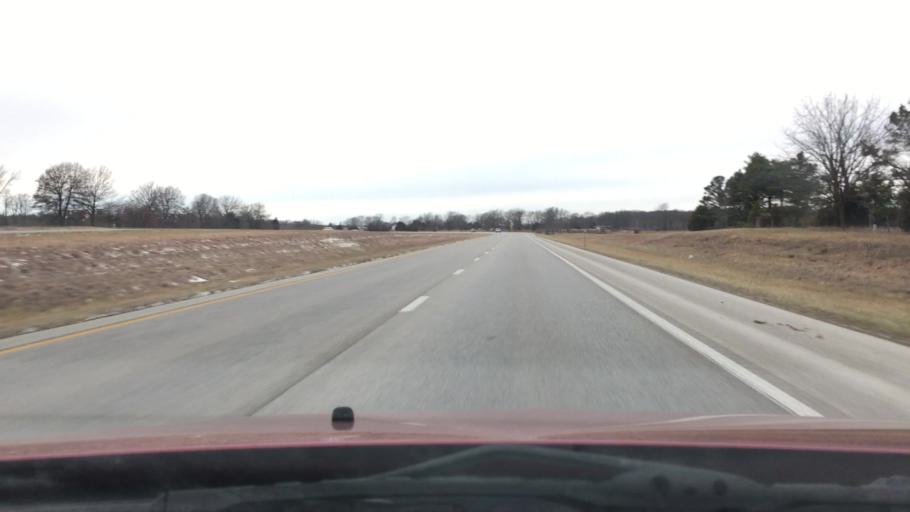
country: US
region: Missouri
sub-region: Webster County
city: Seymour
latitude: 37.1658
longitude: -92.8015
